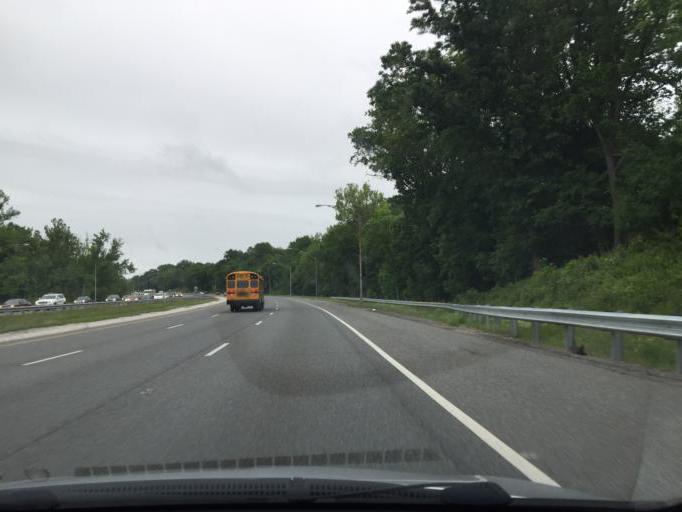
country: US
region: Maryland
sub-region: Baltimore County
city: Mays Chapel
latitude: 39.4011
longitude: -76.6626
